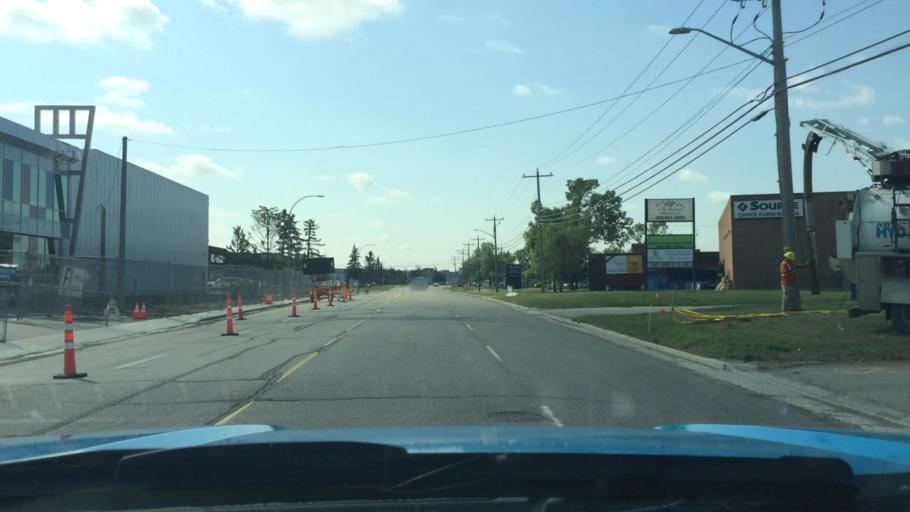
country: CA
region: Alberta
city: Calgary
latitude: 51.0869
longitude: -114.0310
